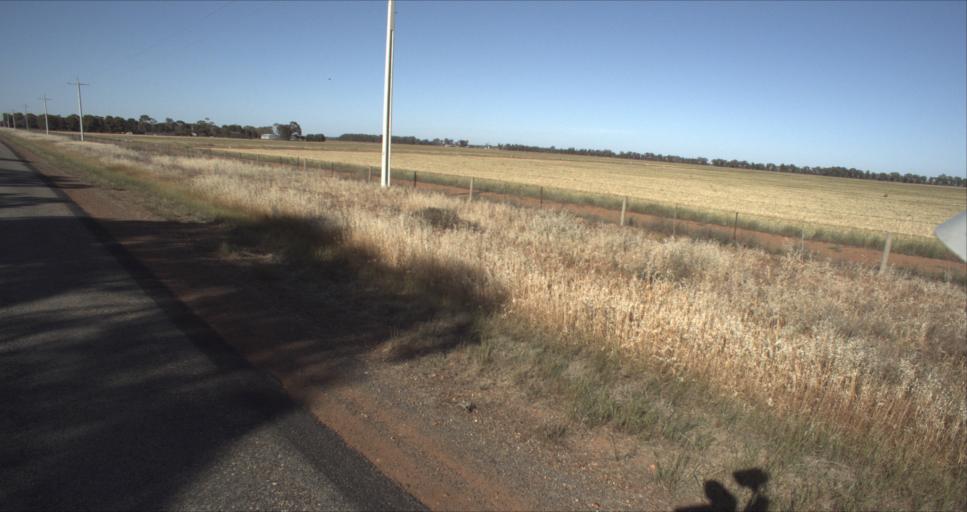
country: AU
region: New South Wales
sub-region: Leeton
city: Leeton
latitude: -34.5795
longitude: 146.2619
